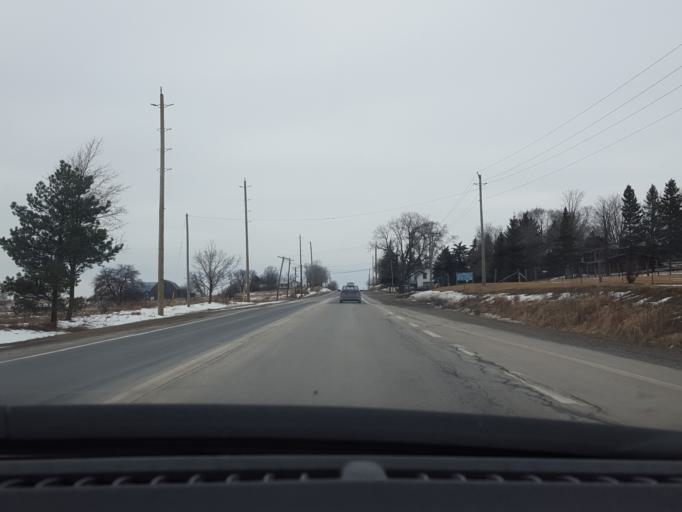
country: CA
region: Ontario
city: Newmarket
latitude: 44.1459
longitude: -79.4264
